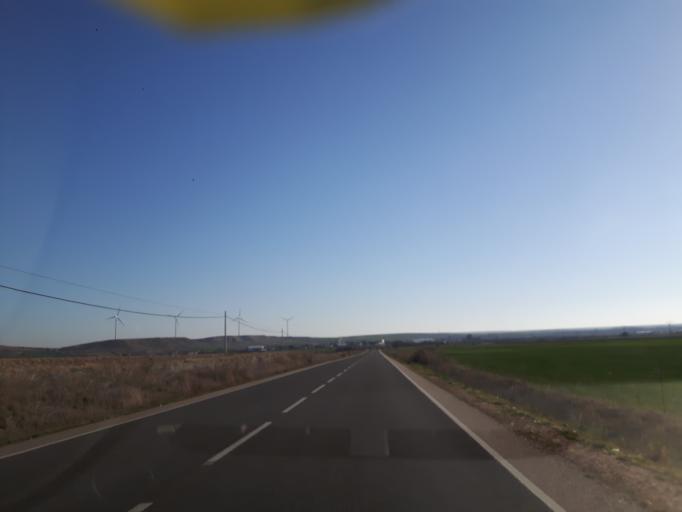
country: ES
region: Castille and Leon
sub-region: Provincia de Salamanca
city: Garcihernandez
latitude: 40.8523
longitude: -5.4485
